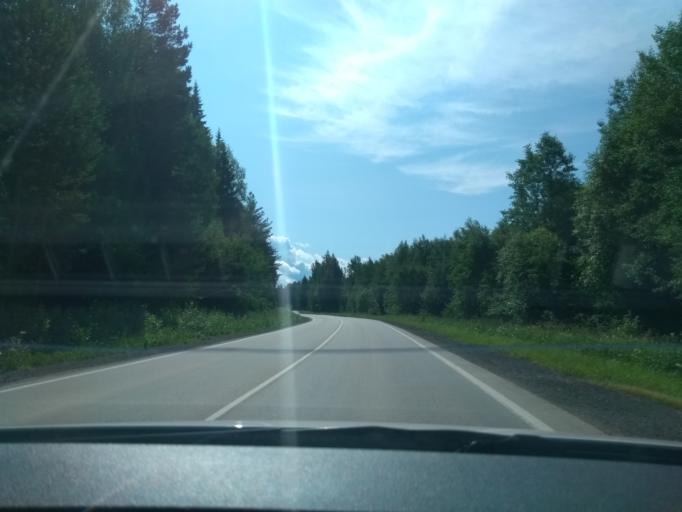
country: RU
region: Perm
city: Bershet'
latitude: 57.8308
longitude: 56.4061
